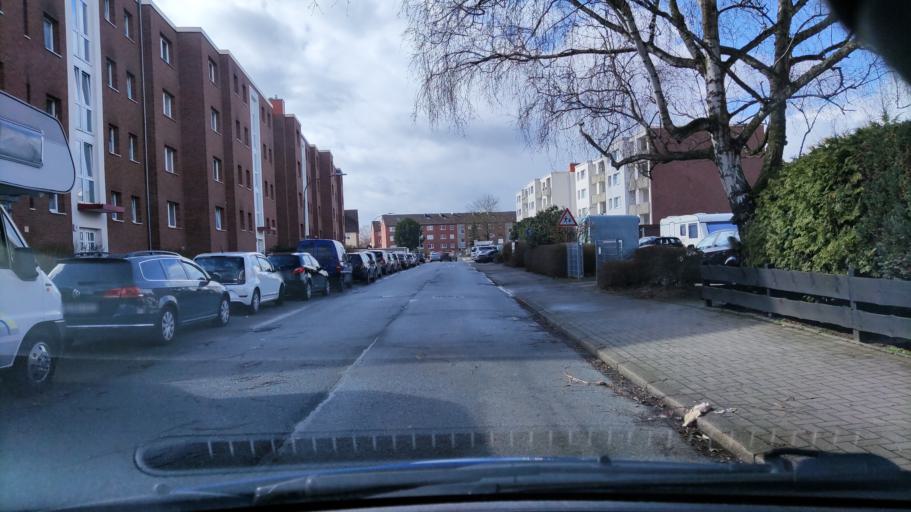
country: DE
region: Lower Saxony
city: Winsen
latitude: 53.3677
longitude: 10.1942
